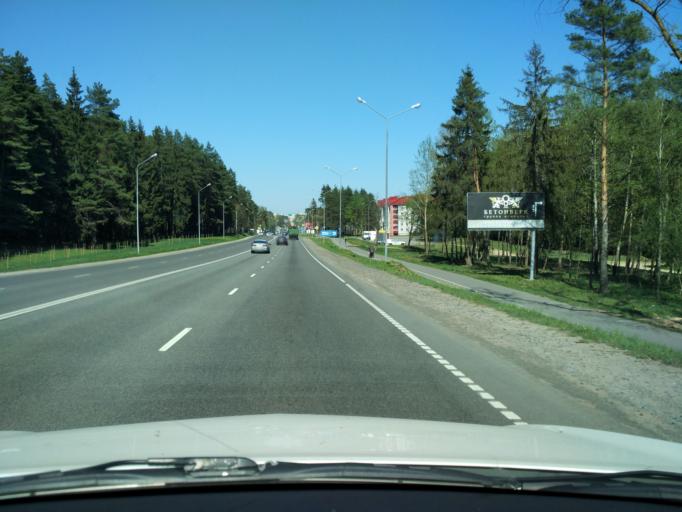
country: BY
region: Minsk
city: Borovlyany
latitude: 53.9864
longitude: 27.6617
